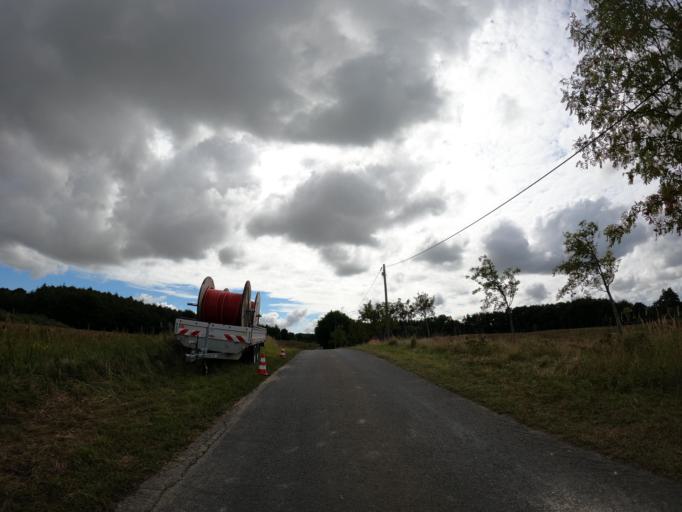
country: DE
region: Mecklenburg-Vorpommern
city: Garz
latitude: 54.3488
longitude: 13.3473
